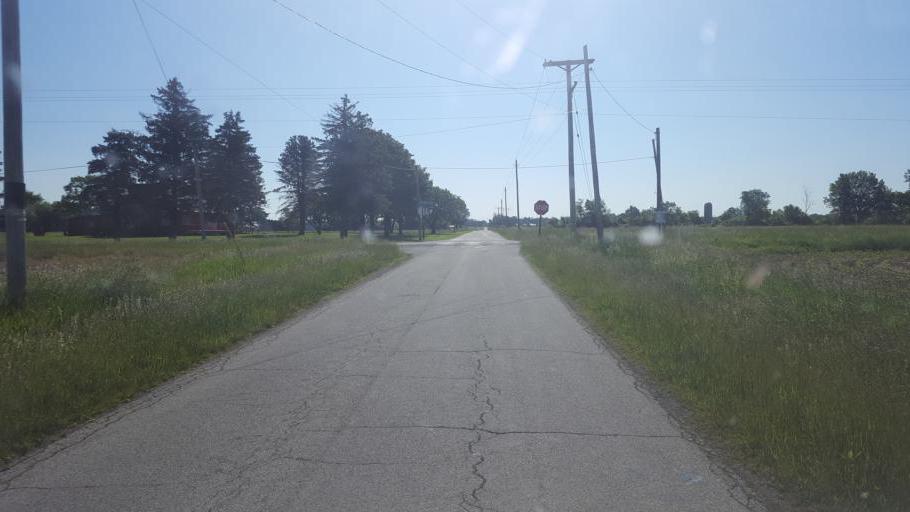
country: US
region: Ohio
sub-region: Crawford County
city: Bucyrus
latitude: 40.7400
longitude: -82.9375
